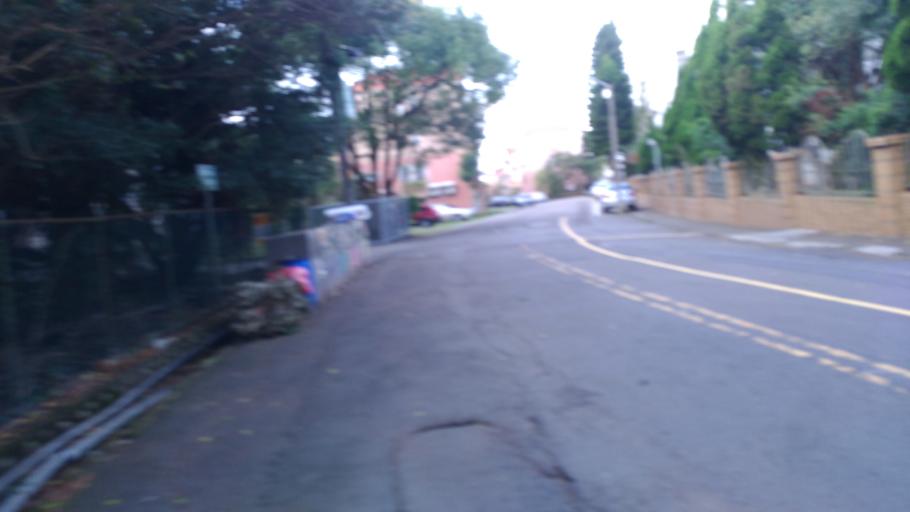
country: TW
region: Taiwan
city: Daxi
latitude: 24.8828
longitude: 121.1735
